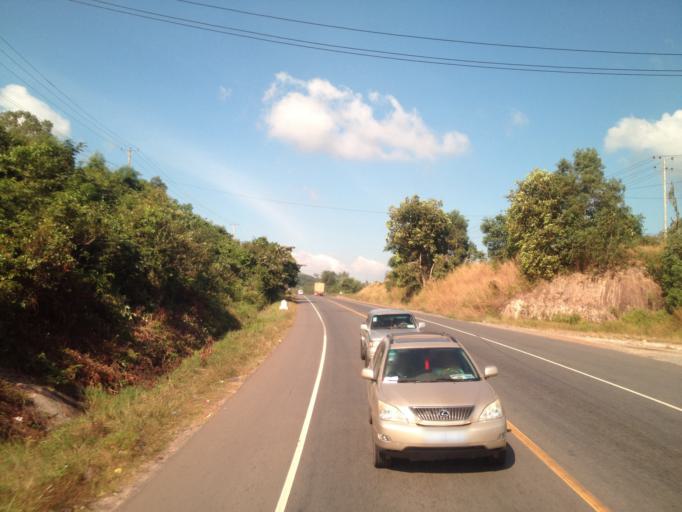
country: KH
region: Preah Sihanouk
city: Sihanoukville
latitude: 10.6057
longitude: 103.6188
